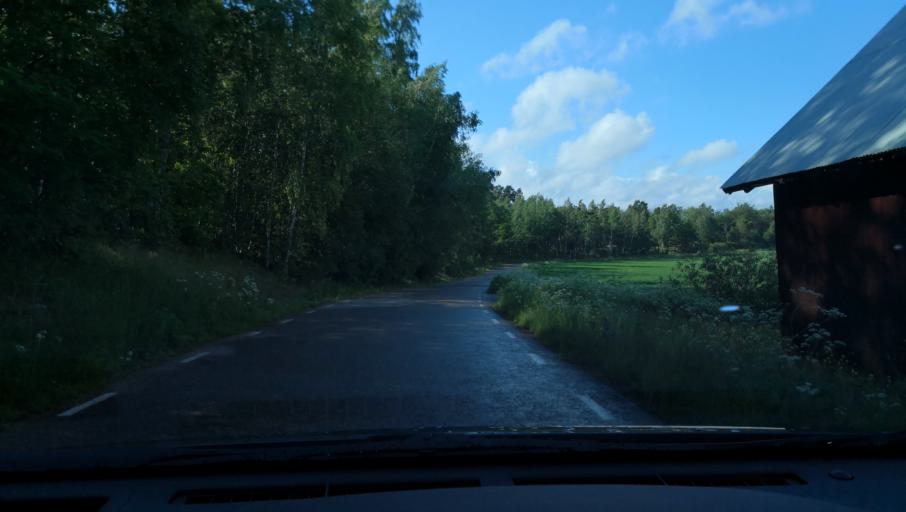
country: SE
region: OErebro
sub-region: Lindesbergs Kommun
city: Fellingsbro
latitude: 59.3093
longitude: 15.6790
